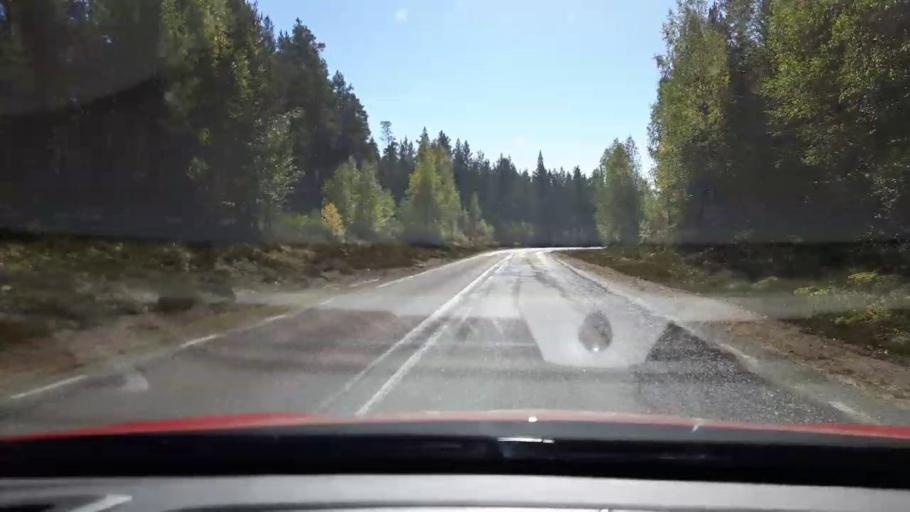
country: SE
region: Jaemtland
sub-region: Harjedalens Kommun
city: Sveg
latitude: 62.1225
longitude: 14.1662
